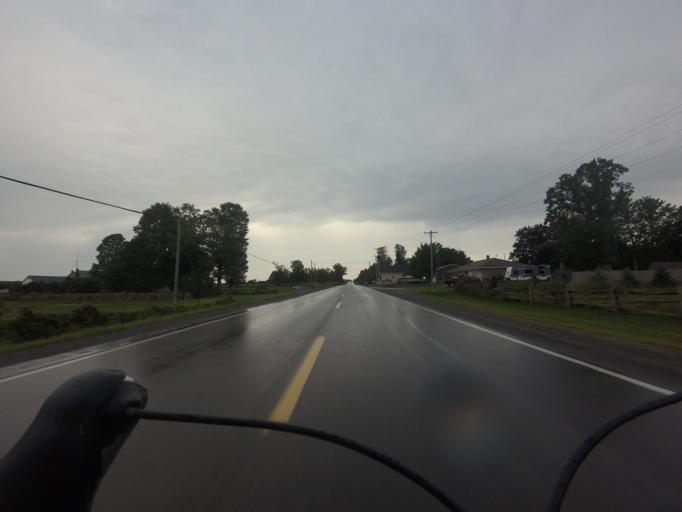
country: CA
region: Ontario
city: Bells Corners
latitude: 45.1973
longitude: -75.6898
